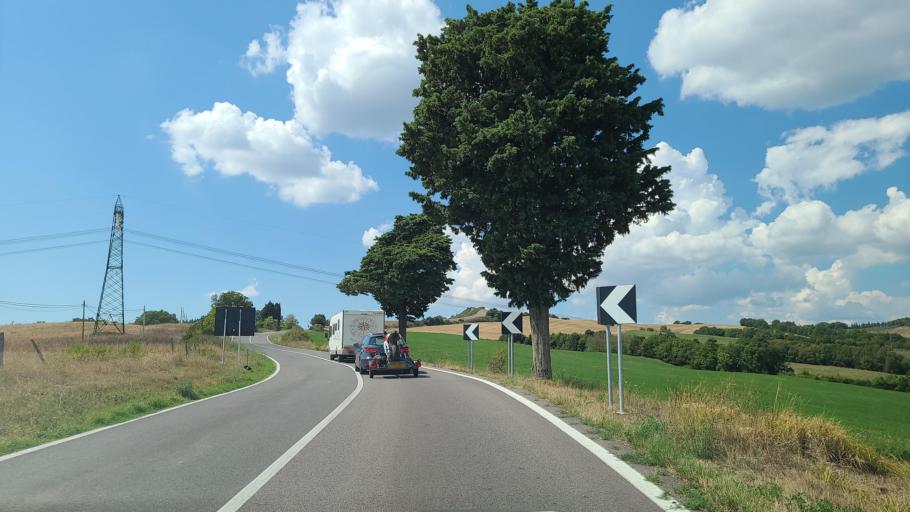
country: IT
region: Tuscany
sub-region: Provincia di Siena
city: San Gimignano
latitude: 43.4017
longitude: 10.9884
